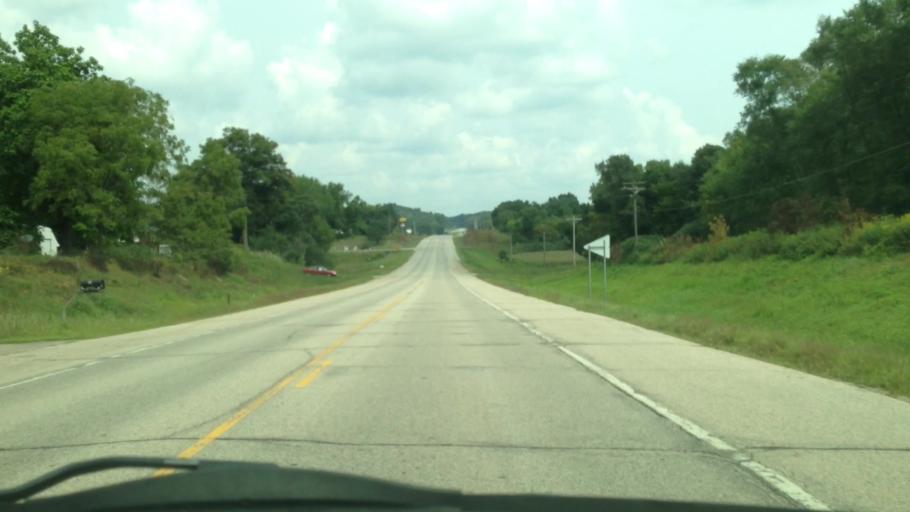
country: US
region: Minnesota
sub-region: Olmsted County
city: Rochester
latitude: 44.0969
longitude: -92.4385
